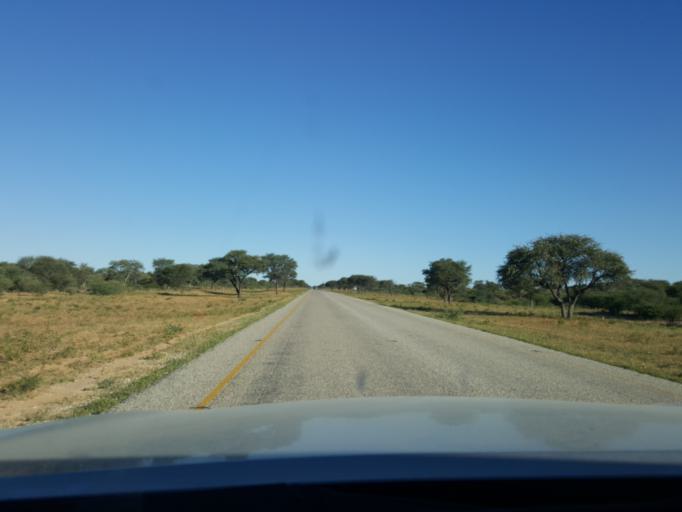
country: BW
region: Kgalagadi
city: Kang
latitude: -24.0328
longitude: 23.0435
